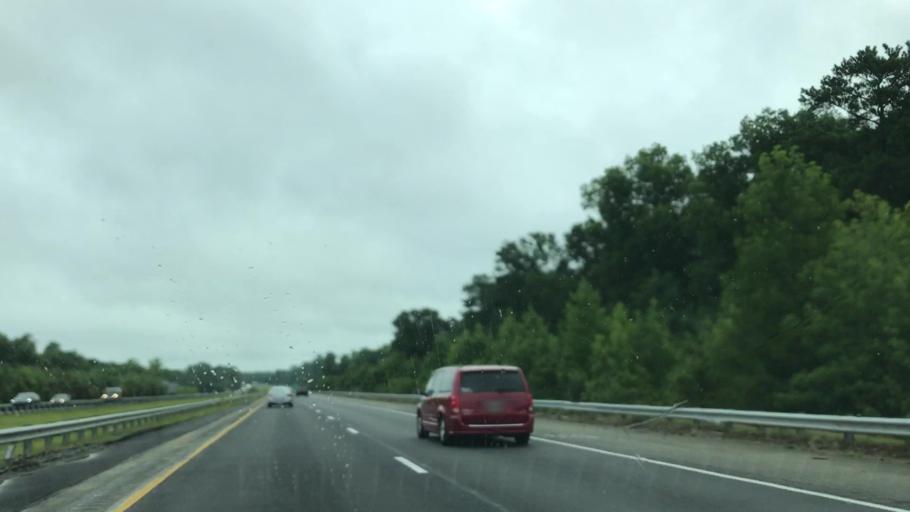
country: US
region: North Carolina
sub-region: Halifax County
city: Roanoke Rapids
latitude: 36.4461
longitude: -77.6241
